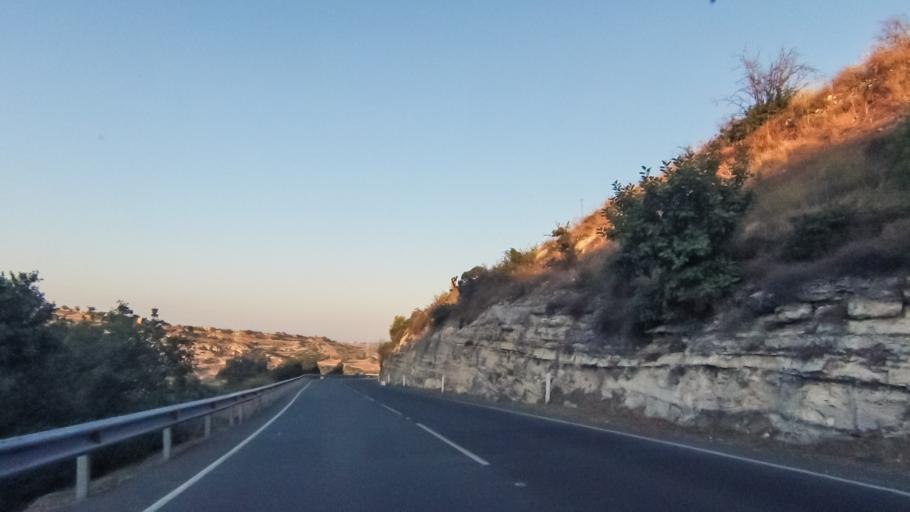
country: CY
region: Limassol
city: Erimi
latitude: 34.6663
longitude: 32.8866
